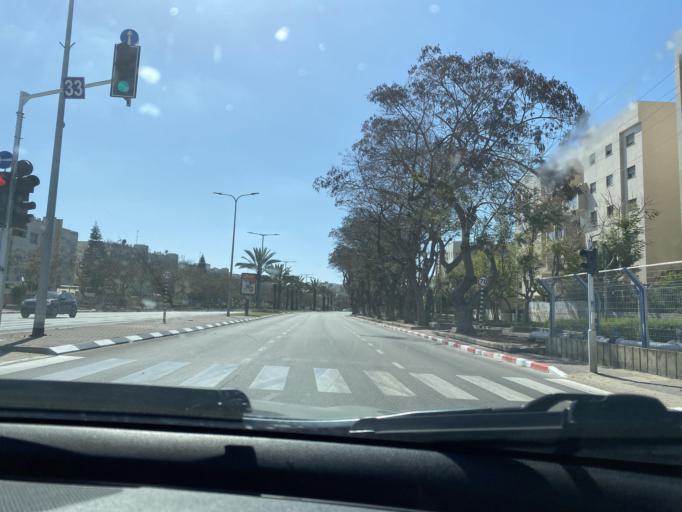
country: IL
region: Southern District
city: Ashqelon
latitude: 31.6737
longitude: 34.5849
